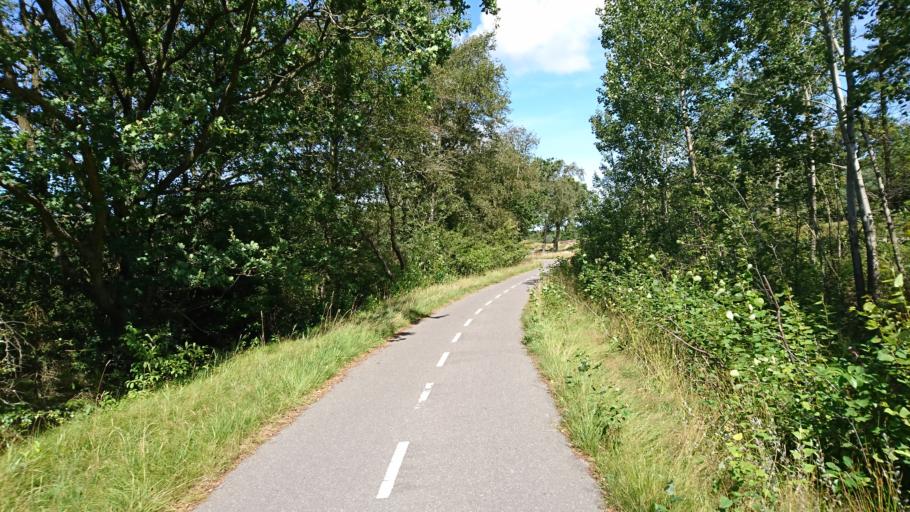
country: DK
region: South Denmark
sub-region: Fano Kommune
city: Nordby
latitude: 55.3975
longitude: 8.4218
